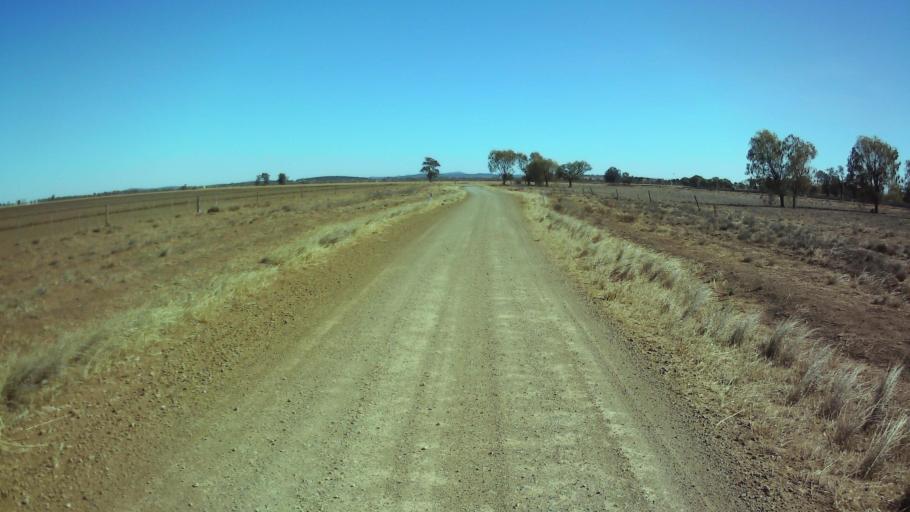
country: AU
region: New South Wales
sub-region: Weddin
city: Grenfell
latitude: -33.8341
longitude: 147.7423
